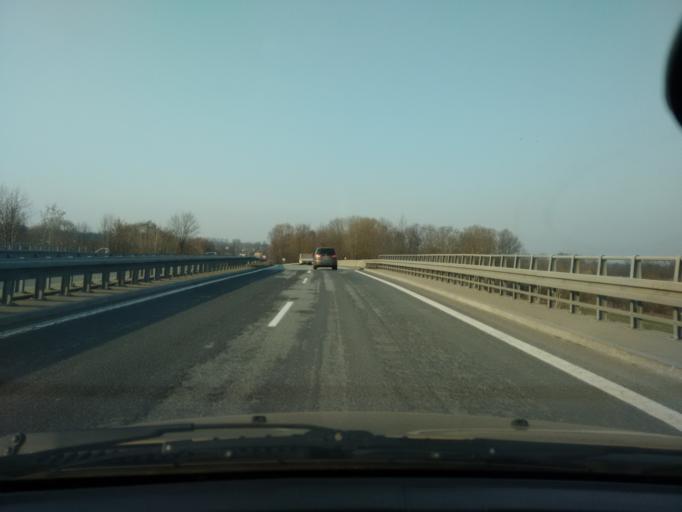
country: PL
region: Silesian Voivodeship
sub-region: Powiat cieszynski
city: Drogomysl
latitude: 49.8857
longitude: 18.7467
